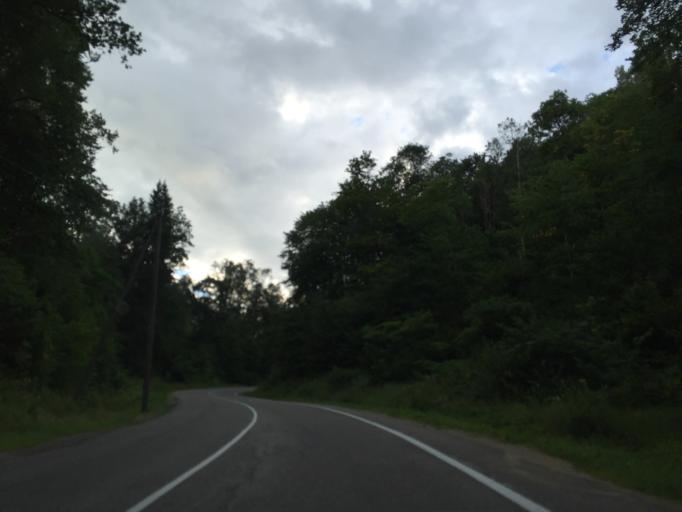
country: LV
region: Sigulda
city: Sigulda
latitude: 57.1823
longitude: 24.8485
